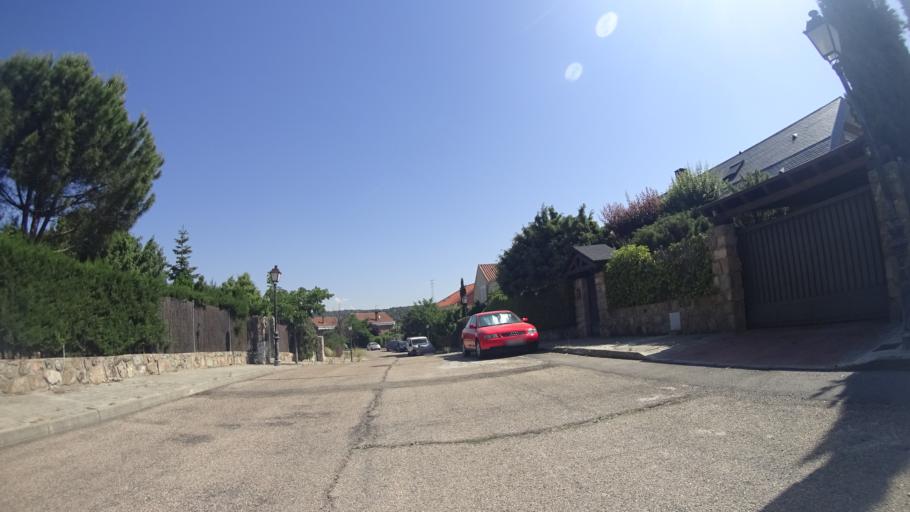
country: ES
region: Madrid
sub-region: Provincia de Madrid
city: Hoyo de Manzanares
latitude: 40.6050
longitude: -3.8982
